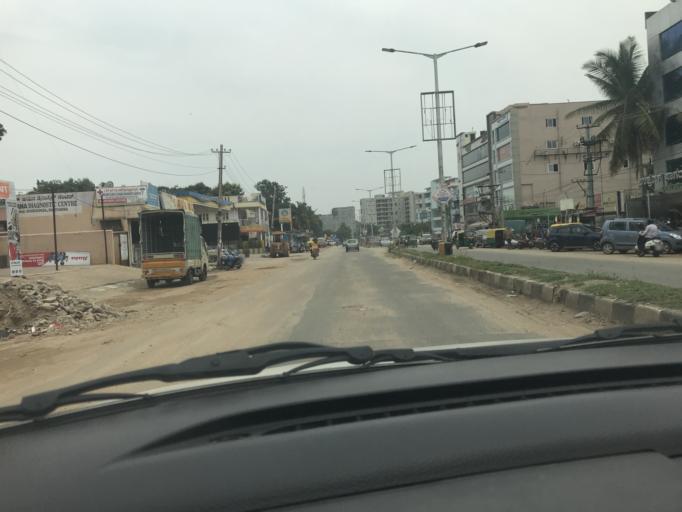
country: IN
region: Karnataka
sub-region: Bangalore Urban
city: Yelahanka
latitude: 13.0599
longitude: 77.6488
